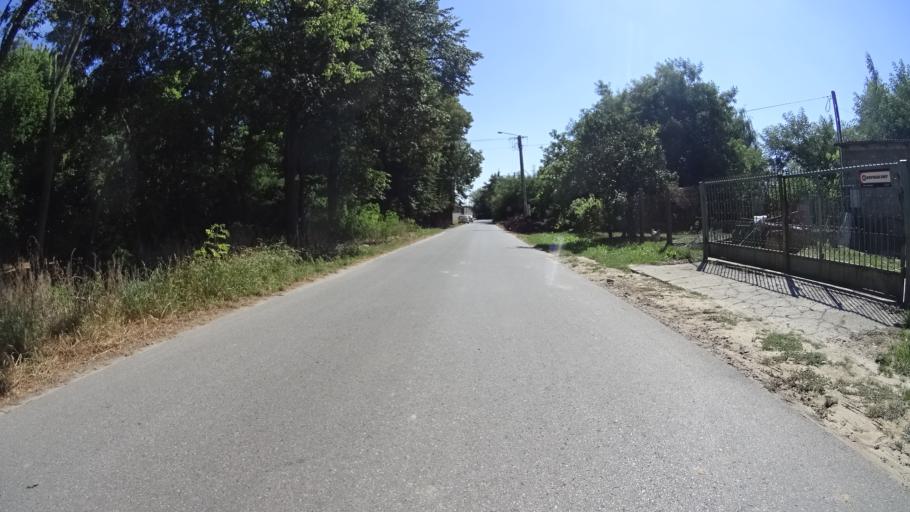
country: PL
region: Masovian Voivodeship
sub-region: Powiat bialobrzeski
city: Bialobrzegi
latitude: 51.6702
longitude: 20.9142
